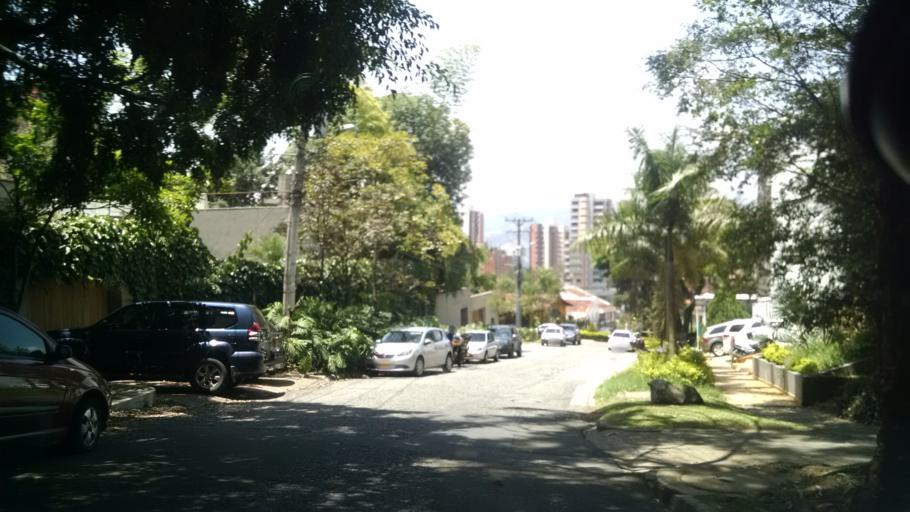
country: CO
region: Antioquia
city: Medellin
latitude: 6.2143
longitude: -75.5613
